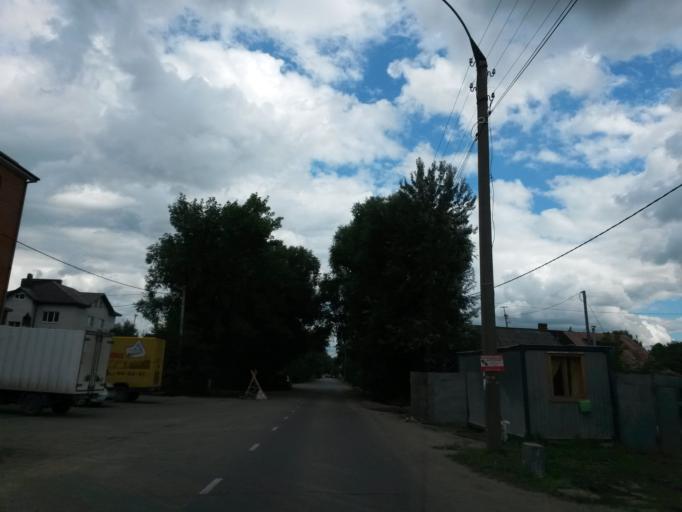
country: RU
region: Jaroslavl
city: Yaroslavl
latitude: 57.6088
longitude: 39.8844
